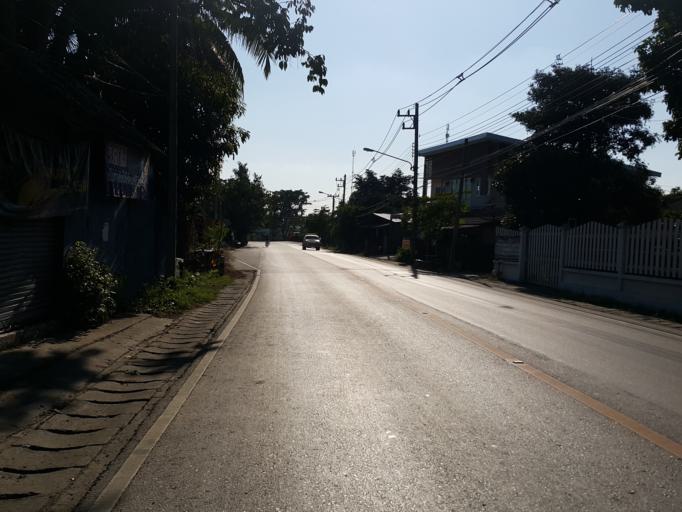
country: TH
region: Chiang Mai
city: San Kamphaeng
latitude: 18.8098
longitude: 99.1194
